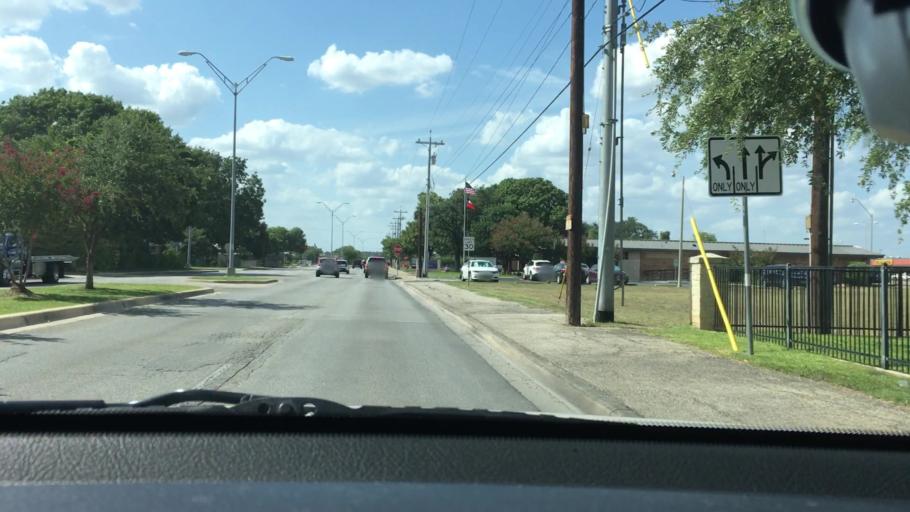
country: US
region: Texas
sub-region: Guadalupe County
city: Schertz
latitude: 29.5569
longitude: -98.2647
